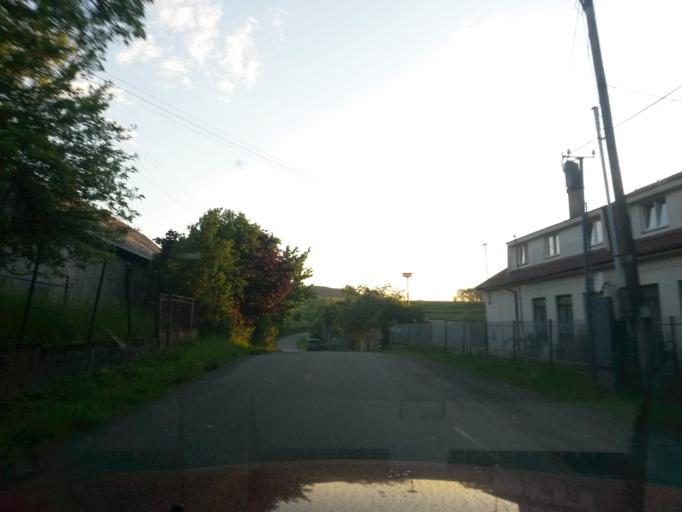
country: UA
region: Zakarpattia
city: Velykyi Bereznyi
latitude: 48.8221
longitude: 22.3529
